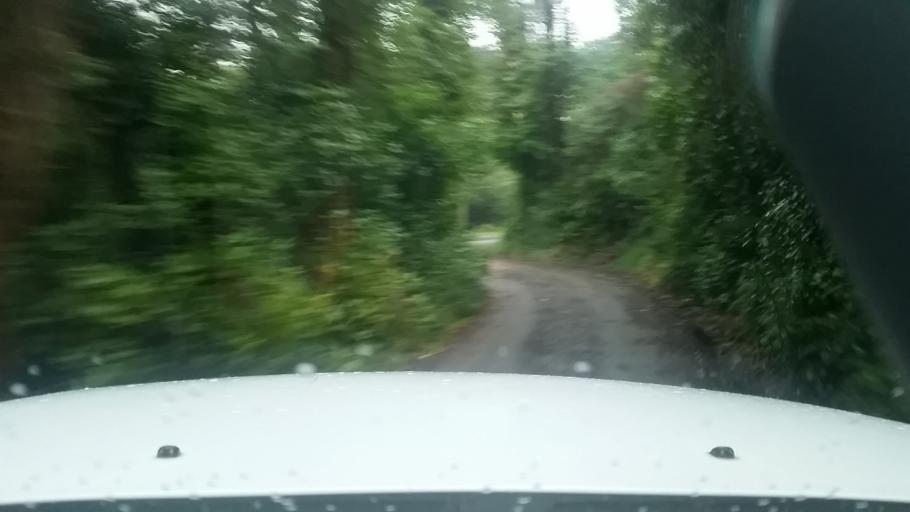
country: NZ
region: Canterbury
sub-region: Christchurch City
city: Christchurch
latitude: -43.8121
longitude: 172.8933
